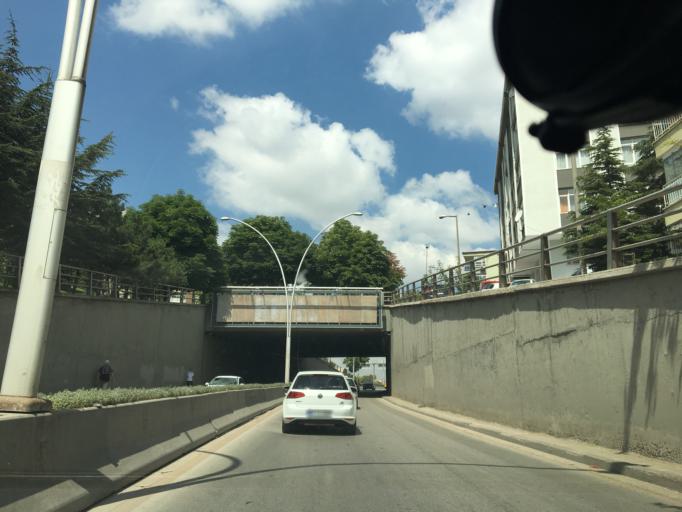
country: TR
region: Ankara
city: Ankara
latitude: 39.8955
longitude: 32.8485
